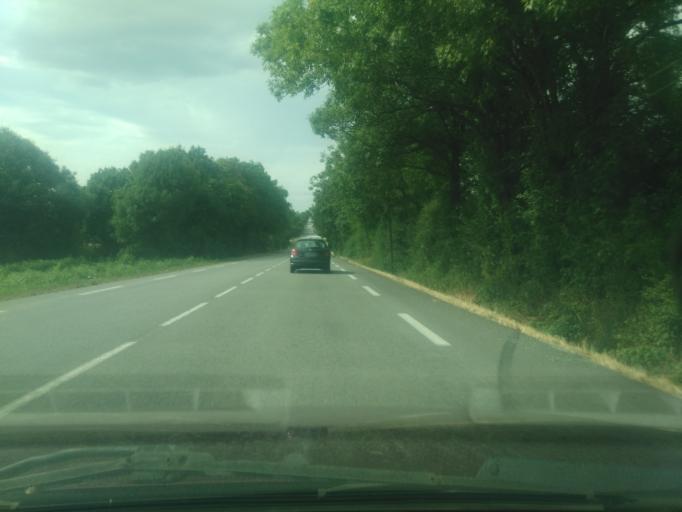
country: FR
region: Pays de la Loire
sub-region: Departement de la Vendee
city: Sainte-Cecile
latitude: 46.7738
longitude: -1.1124
